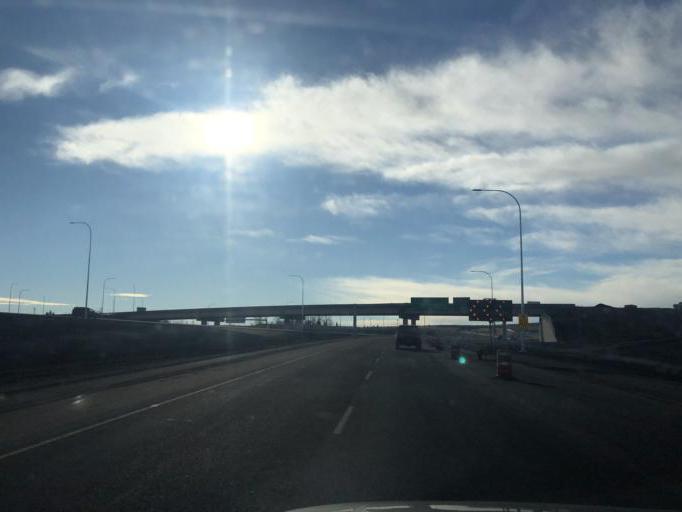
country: CA
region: Alberta
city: Calgary
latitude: 51.0031
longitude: -114.1668
